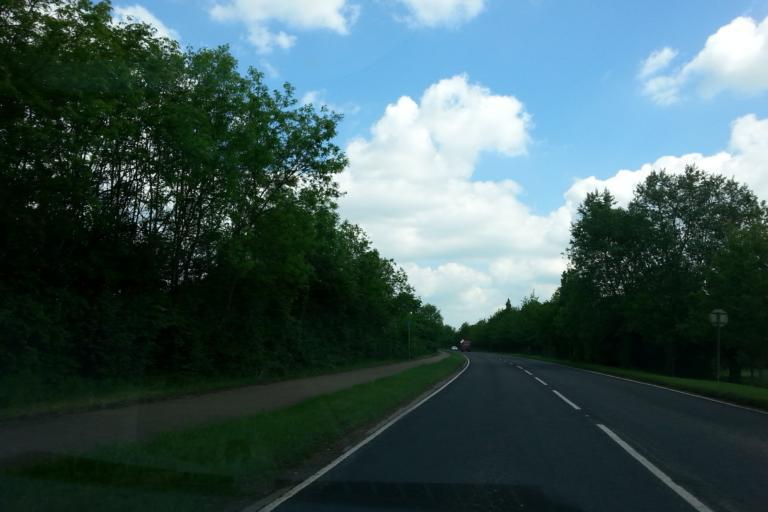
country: GB
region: England
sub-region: Cambridgeshire
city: Yaxley
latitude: 52.5121
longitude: -0.2736
